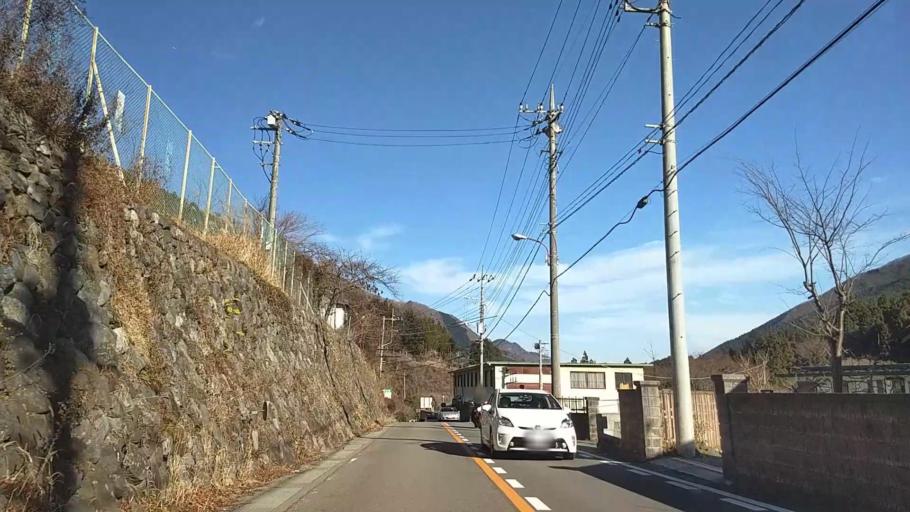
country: JP
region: Yamanashi
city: Uenohara
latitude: 35.5297
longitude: 139.0412
